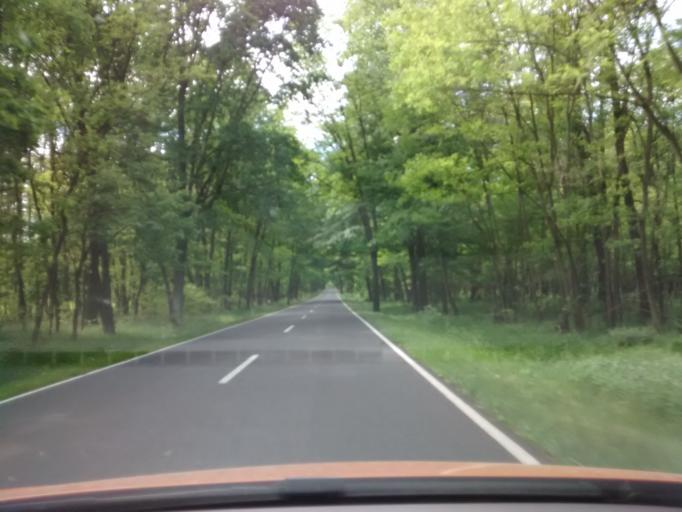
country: DE
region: Brandenburg
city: Ihlow
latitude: 51.9902
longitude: 13.2737
